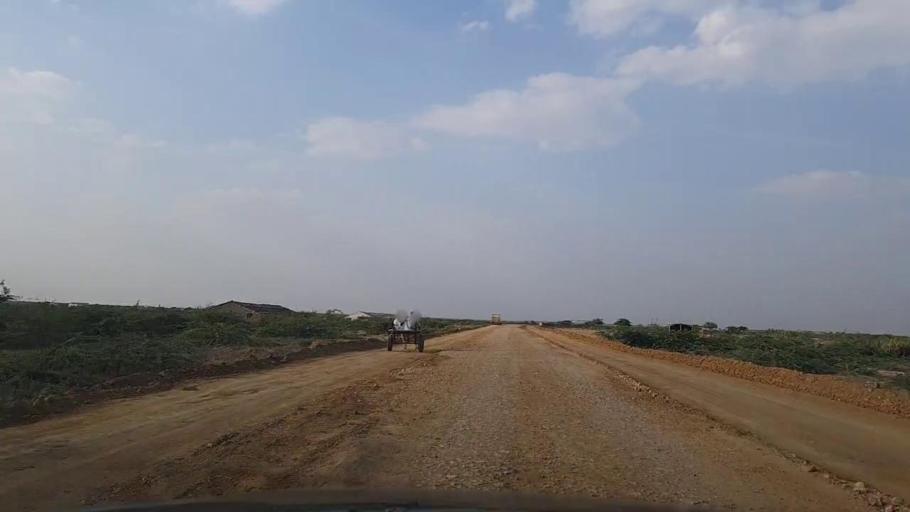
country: PK
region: Sindh
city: Gharo
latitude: 24.7861
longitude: 67.7451
